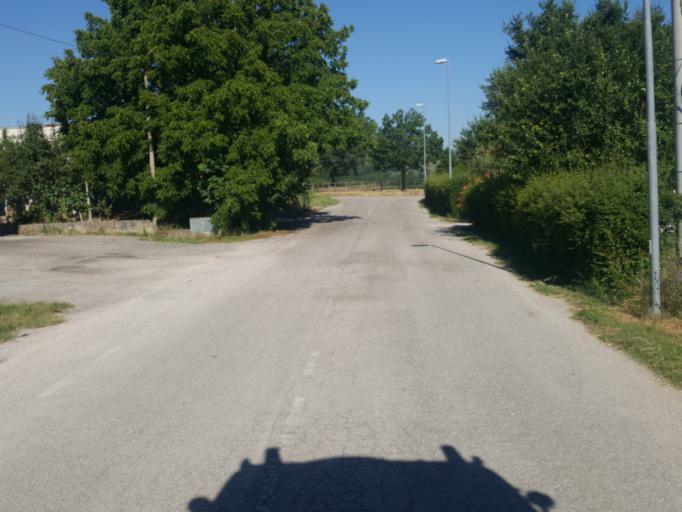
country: IT
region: The Marches
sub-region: Provincia di Pesaro e Urbino
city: Montecalvo in Foglia
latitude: 43.7859
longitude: 12.6314
